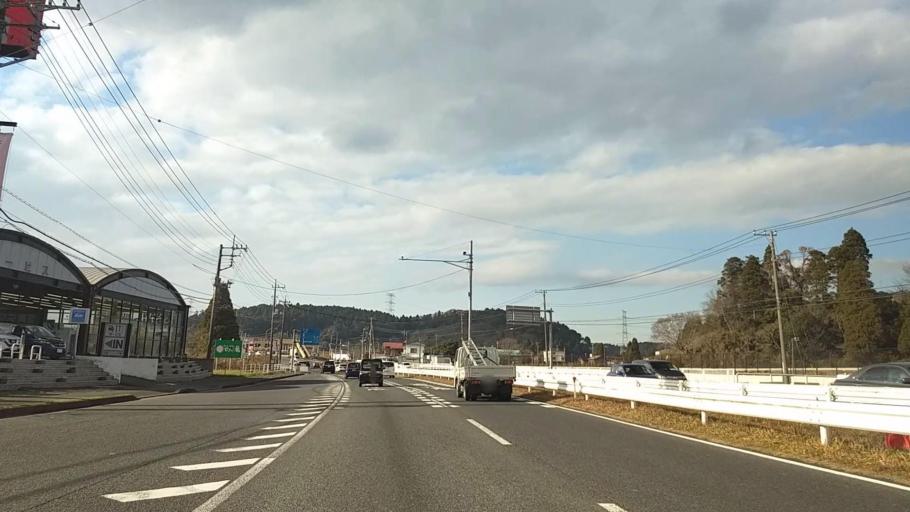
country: JP
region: Chiba
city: Togane
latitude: 35.5741
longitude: 140.3278
